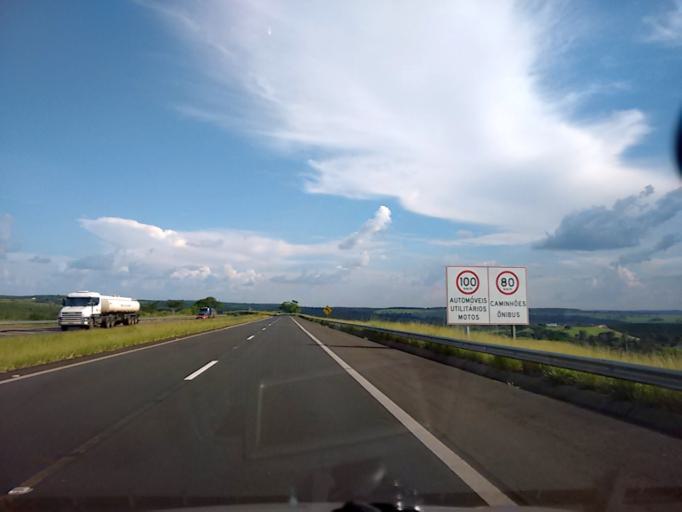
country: BR
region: Sao Paulo
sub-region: Duartina
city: Duartina
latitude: -22.3153
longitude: -49.4933
